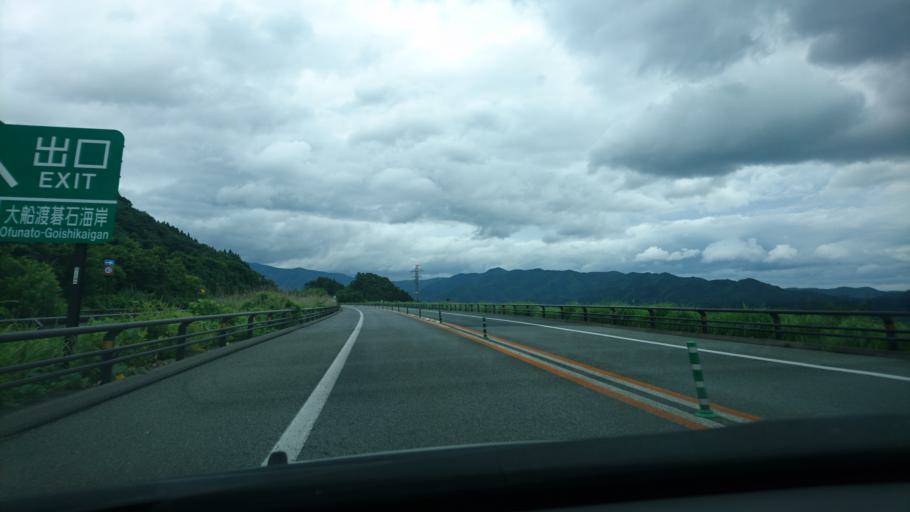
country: JP
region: Iwate
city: Ofunato
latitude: 39.0326
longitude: 141.7115
